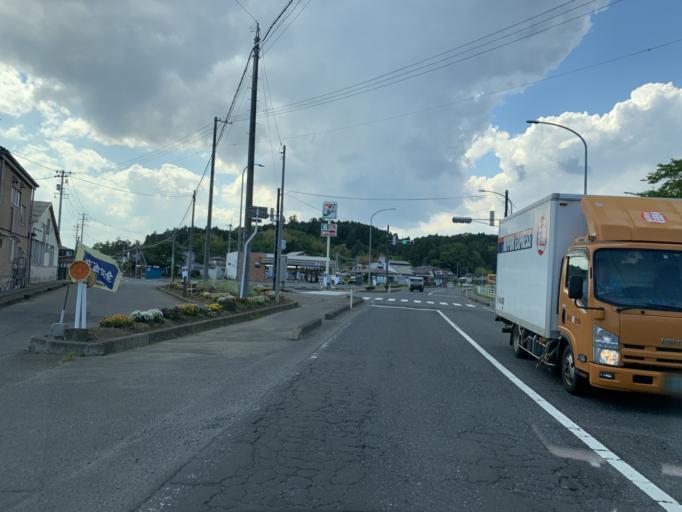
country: JP
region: Miyagi
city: Wakuya
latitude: 38.5442
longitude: 141.1438
